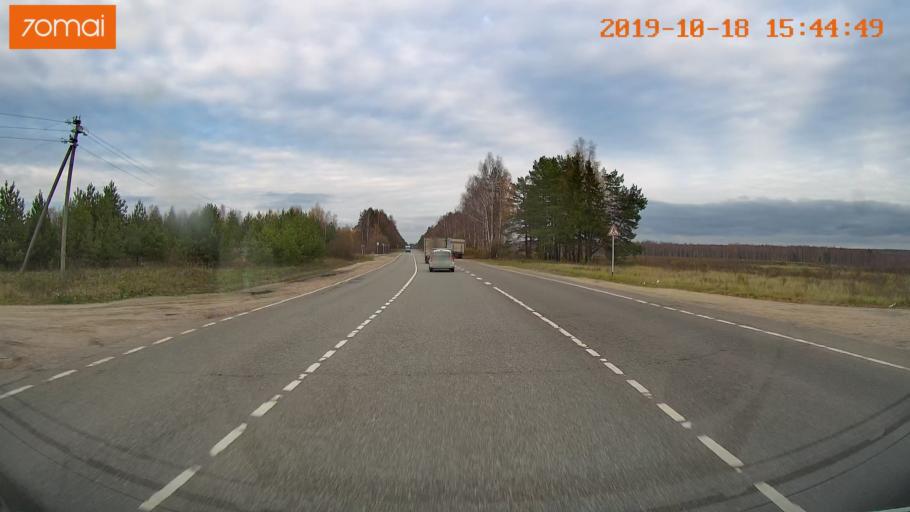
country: RU
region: Vladimir
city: Golovino
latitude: 55.9856
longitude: 40.5556
